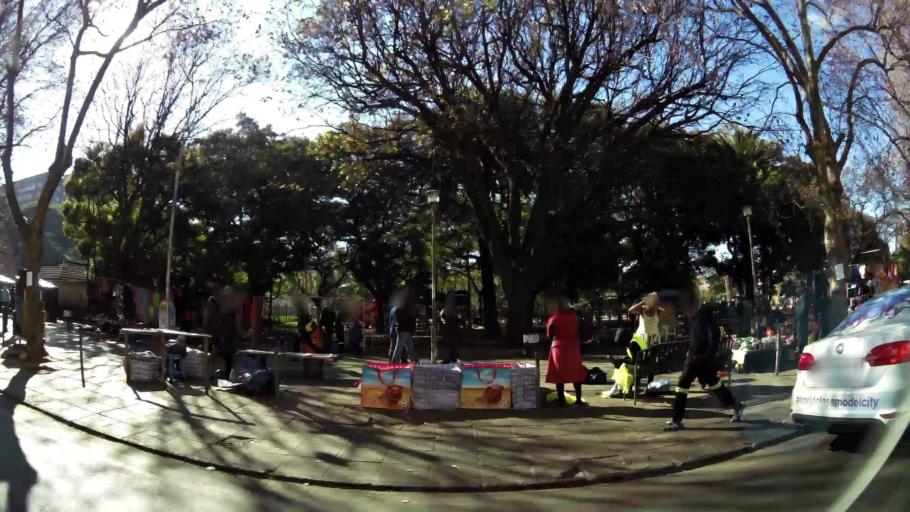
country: ZA
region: Gauteng
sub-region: City of Johannesburg Metropolitan Municipality
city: Johannesburg
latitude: -26.1957
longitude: 28.0457
